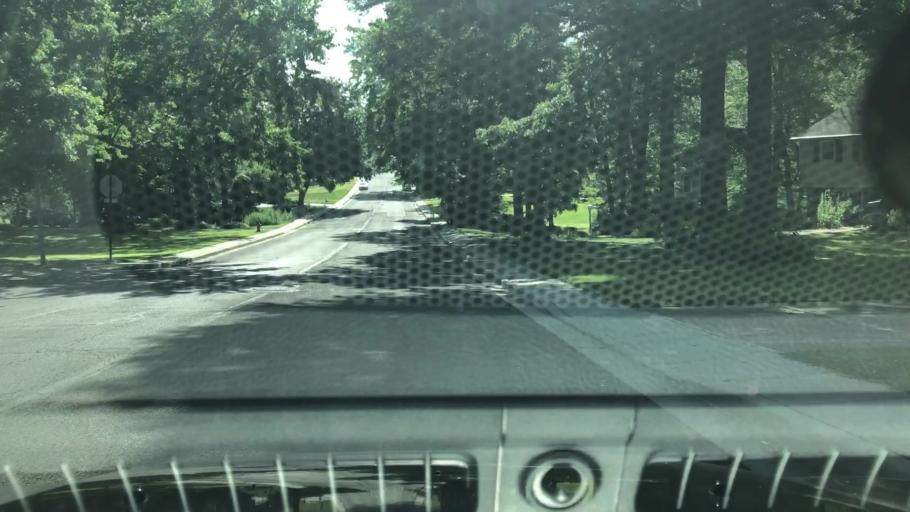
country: US
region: Pennsylvania
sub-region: Bucks County
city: Fairless Hills
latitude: 40.1833
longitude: -74.8458
